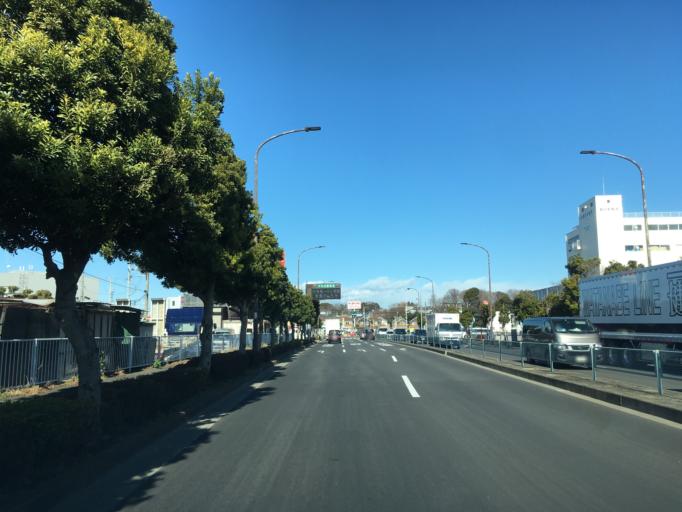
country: JP
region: Tokyo
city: Kokubunji
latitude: 35.6747
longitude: 139.4474
